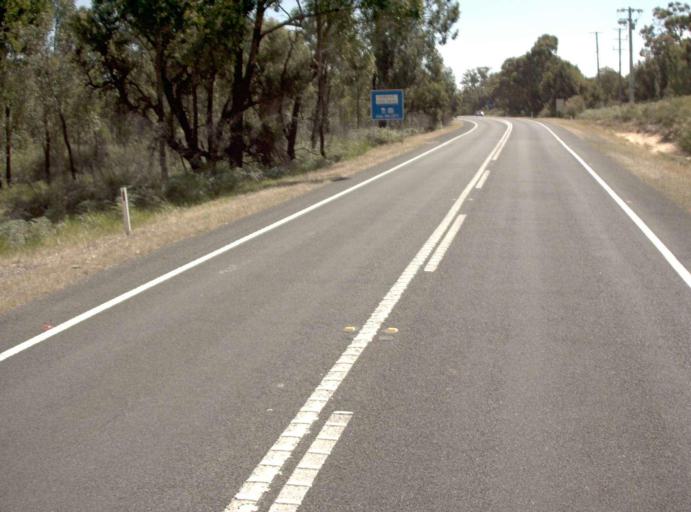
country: AU
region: Victoria
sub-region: Wellington
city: Sale
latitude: -37.9164
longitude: 147.2929
